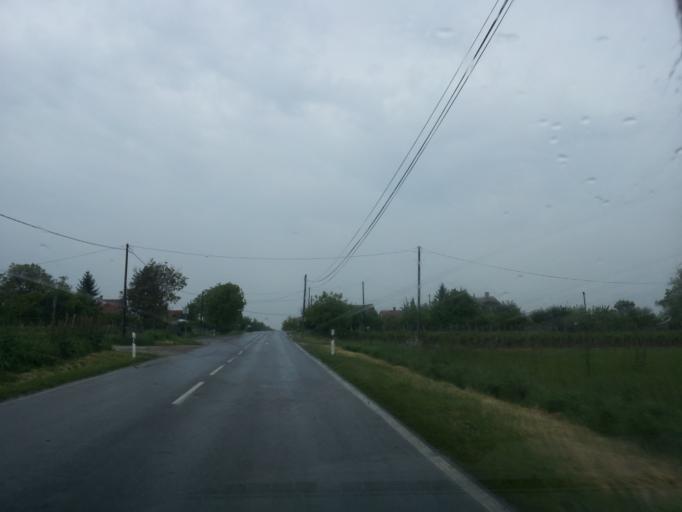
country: HU
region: Tolna
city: Szekszard
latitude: 46.3019
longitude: 18.6899
